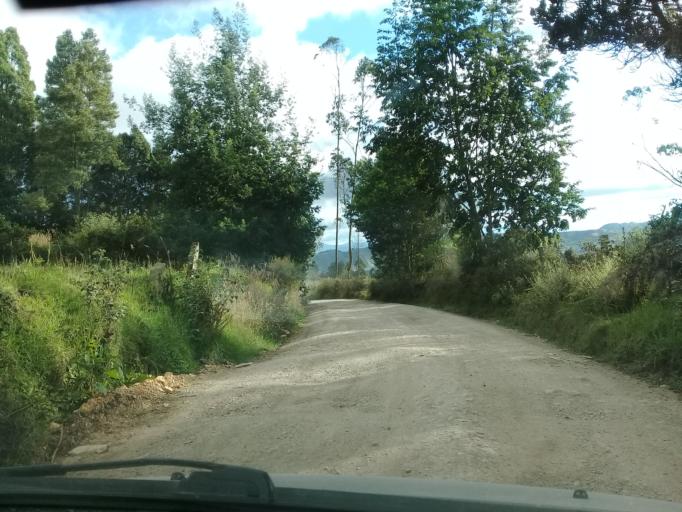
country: CO
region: Cundinamarca
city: Villapinzon
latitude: 5.2363
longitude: -73.6507
